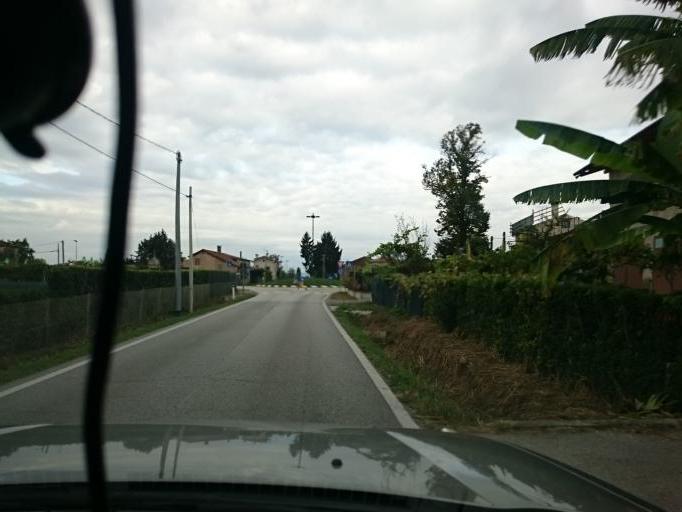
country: IT
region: Veneto
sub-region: Provincia di Padova
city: Mestrino
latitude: 45.4295
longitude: 11.7385
